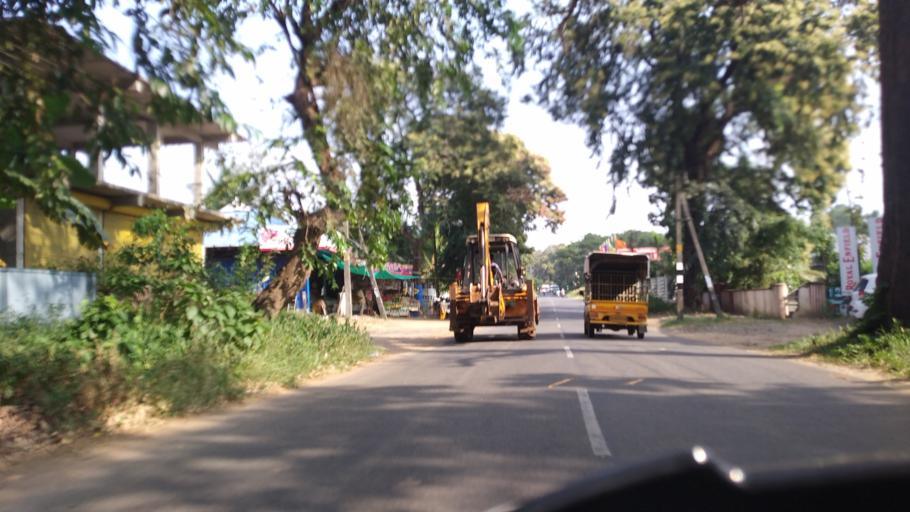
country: IN
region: Kerala
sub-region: Thrissur District
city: Chelakara
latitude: 10.5979
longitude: 76.4990
